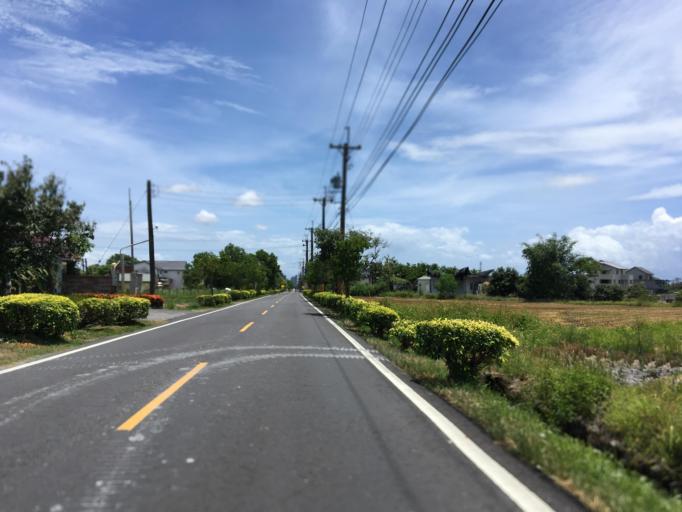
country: TW
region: Taiwan
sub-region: Yilan
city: Yilan
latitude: 24.6562
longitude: 121.7310
